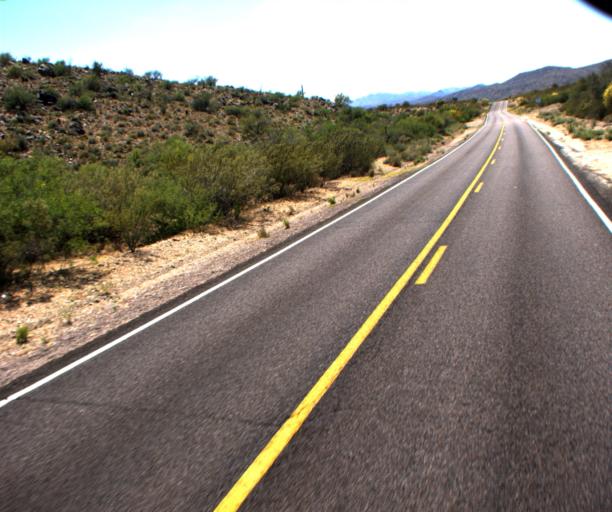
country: US
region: Arizona
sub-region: Yavapai County
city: Bagdad
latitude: 34.4806
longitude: -113.1977
